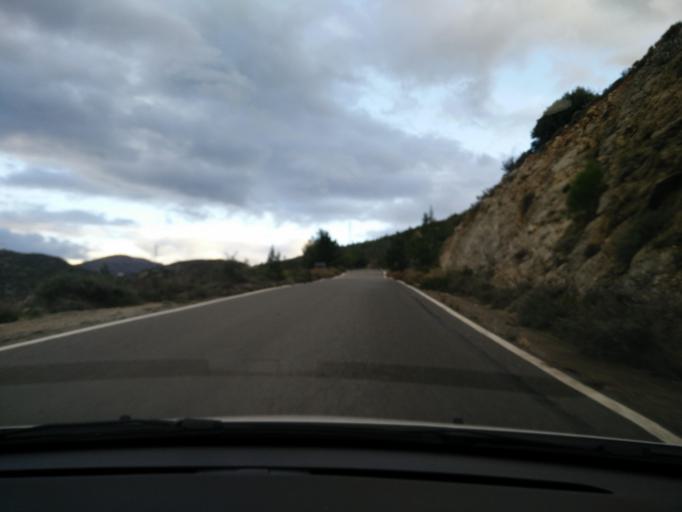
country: GR
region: Crete
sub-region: Nomos Lasithiou
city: Gra Liyia
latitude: 35.0906
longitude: 25.6964
